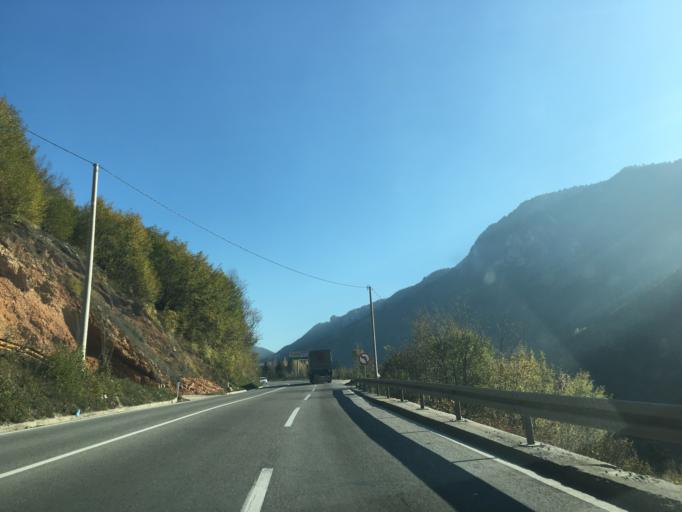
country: BA
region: Federation of Bosnia and Herzegovina
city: Kobilja Glava
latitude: 43.8556
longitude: 18.4578
